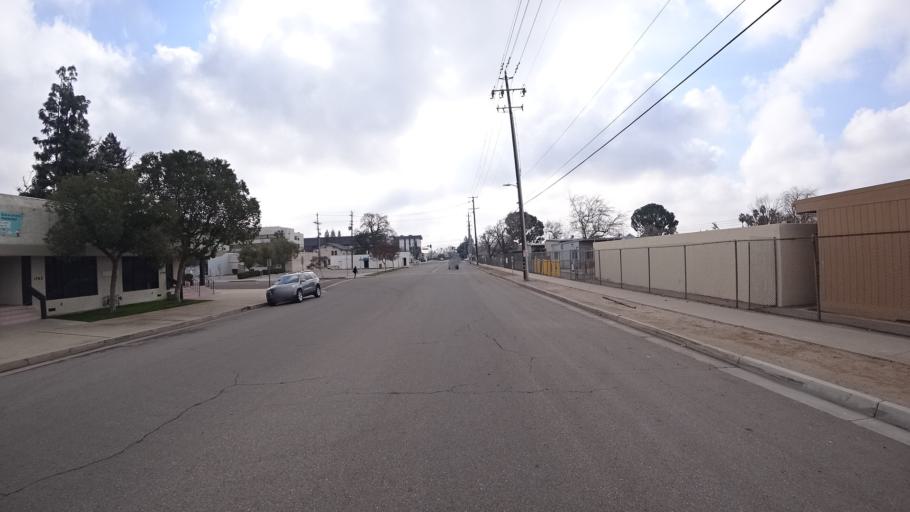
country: US
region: California
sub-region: Kern County
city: Bakersfield
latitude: 35.3747
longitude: -119.0294
